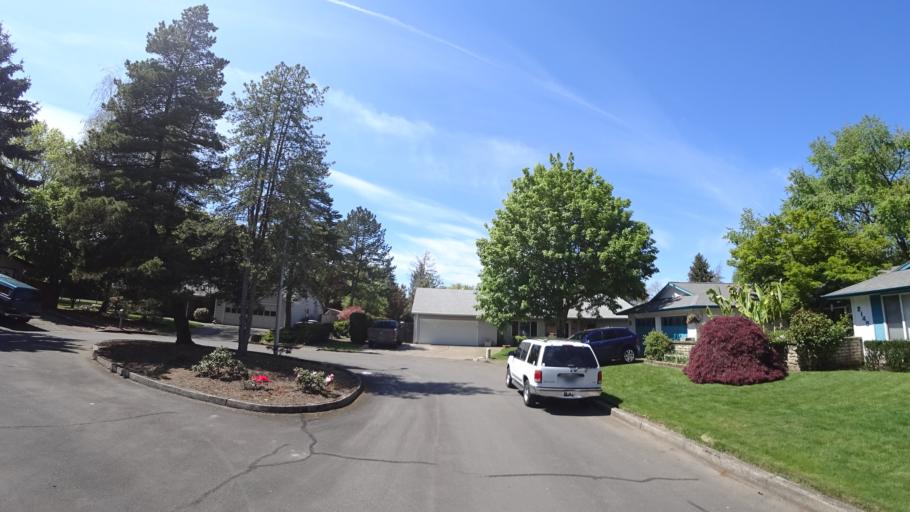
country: US
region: Oregon
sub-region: Washington County
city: Hillsboro
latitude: 45.4999
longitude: -122.9605
